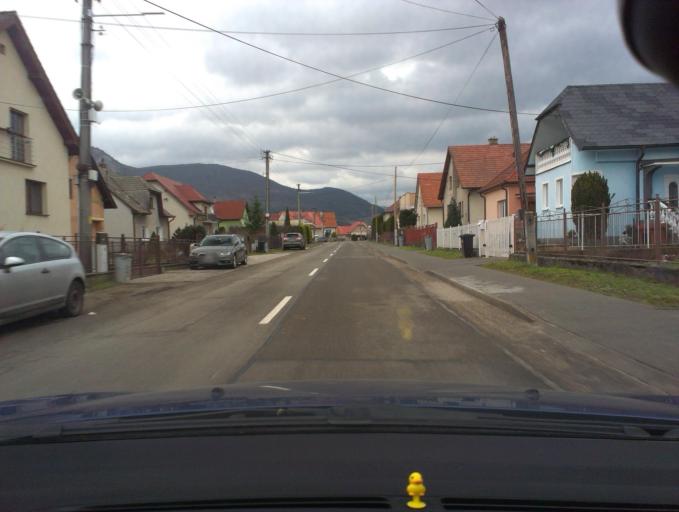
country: SK
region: Nitriansky
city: Trencianske Teplice
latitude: 48.8984
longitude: 18.2171
